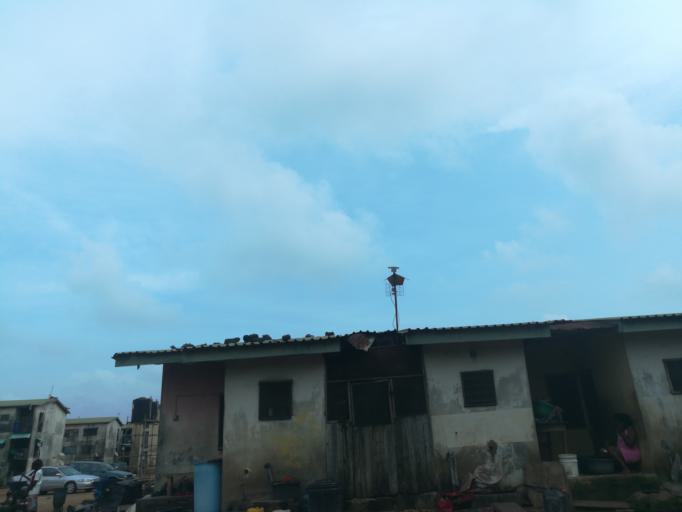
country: NG
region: Lagos
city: Oshodi
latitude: 6.5689
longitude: 3.3583
